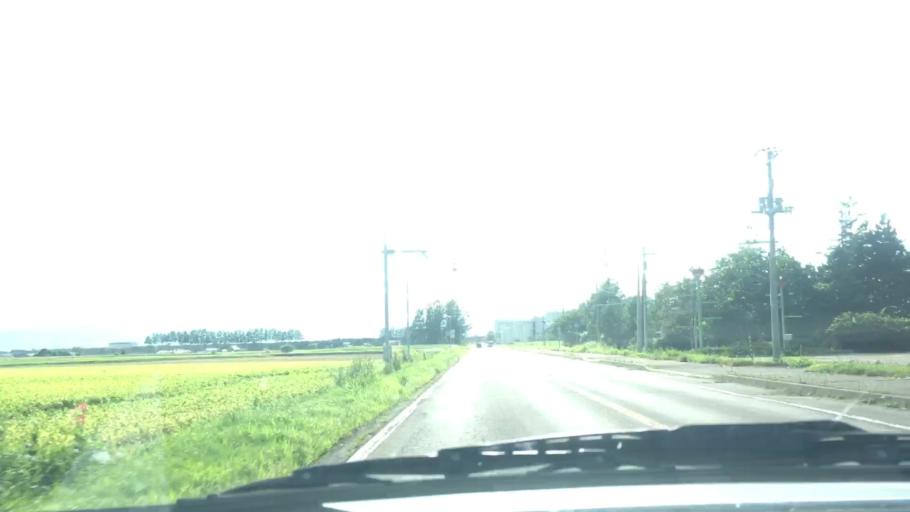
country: JP
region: Hokkaido
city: Otofuke
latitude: 43.1648
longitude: 143.2622
